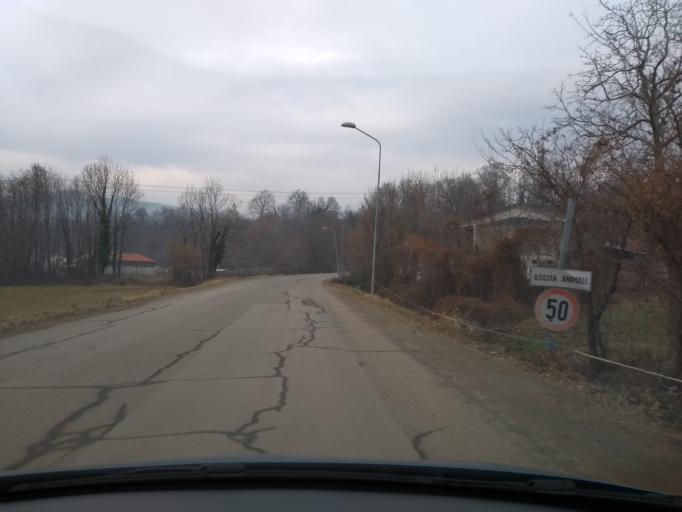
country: IT
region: Piedmont
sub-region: Provincia di Torino
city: Mathi
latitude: 45.2655
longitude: 7.5476
